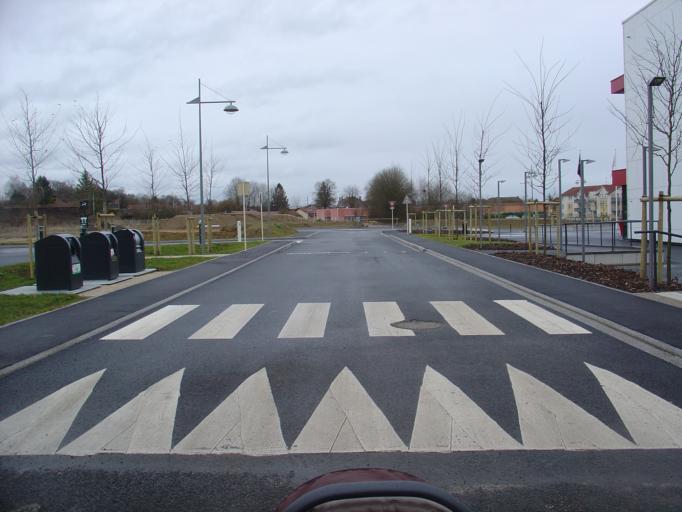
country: FR
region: Lorraine
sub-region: Departement de Meurthe-et-Moselle
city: Toul
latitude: 48.6802
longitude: 5.8884
